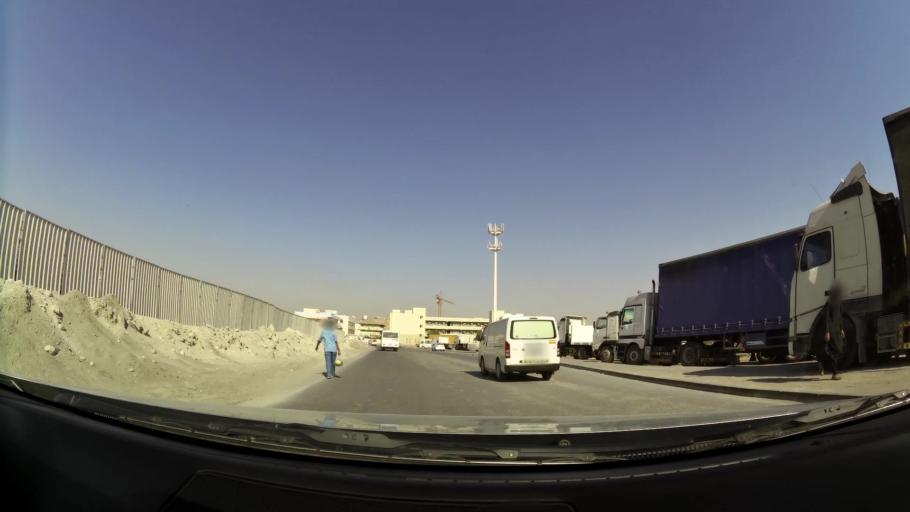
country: AE
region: Dubai
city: Dubai
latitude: 25.0038
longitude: 55.1047
